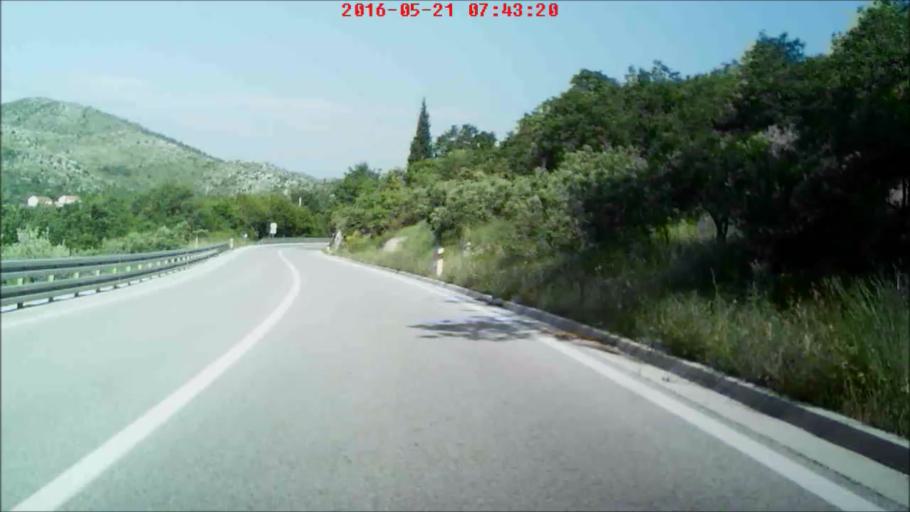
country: HR
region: Dubrovacko-Neretvanska
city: Podgora
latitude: 42.8129
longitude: 17.7911
